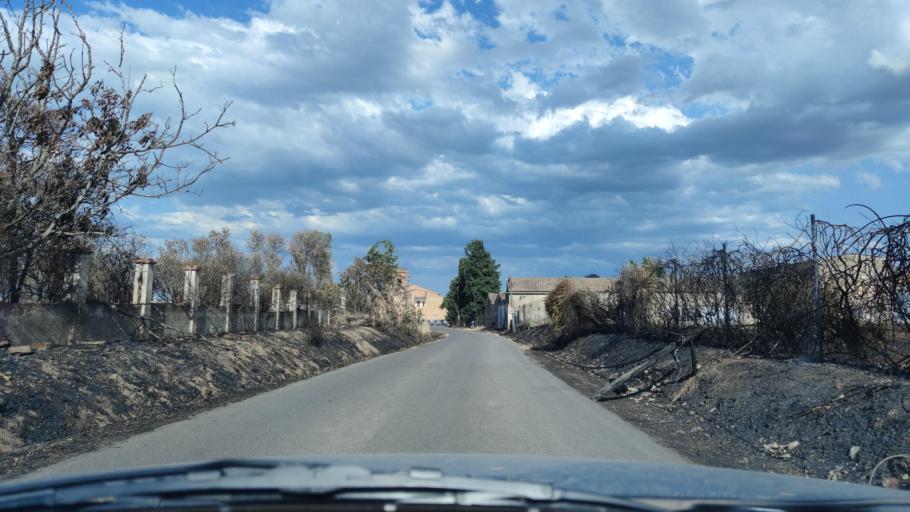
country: ES
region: Catalonia
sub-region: Provincia de Lleida
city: Lleida
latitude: 41.6313
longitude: 0.5902
